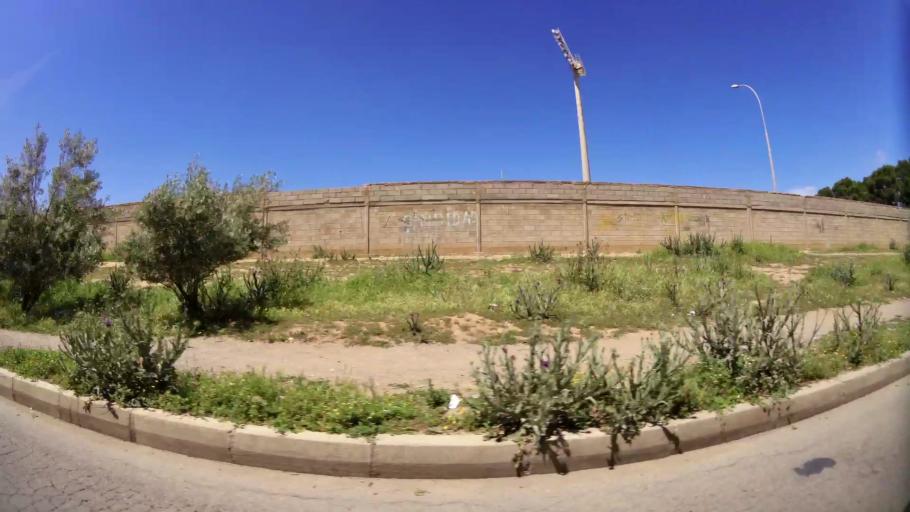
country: MA
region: Oriental
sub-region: Oujda-Angad
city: Oujda
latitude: 34.6605
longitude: -1.9336
